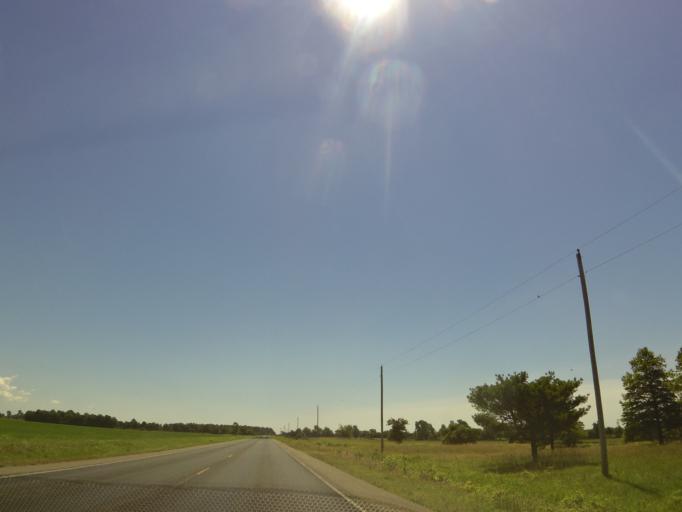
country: US
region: Missouri
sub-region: New Madrid County
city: Lilbourn
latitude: 36.5548
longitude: -89.6790
